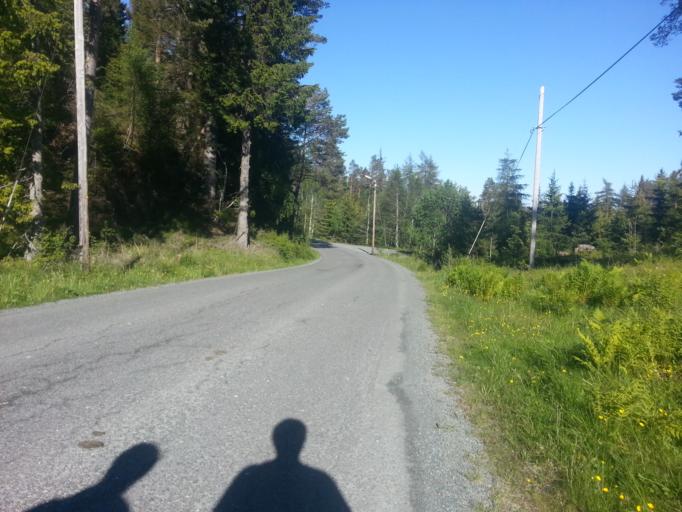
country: NO
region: Sor-Trondelag
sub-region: Trondheim
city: Trondheim
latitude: 63.4218
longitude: 10.3217
